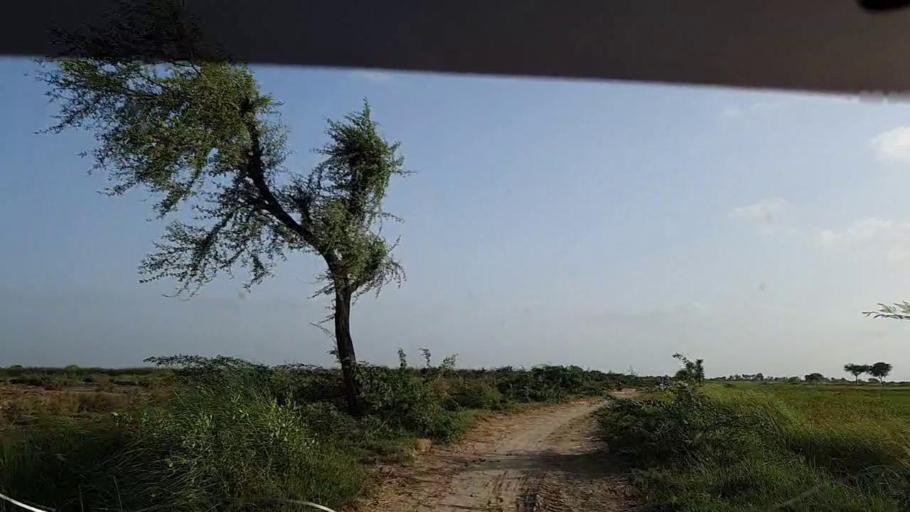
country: PK
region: Sindh
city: Badin
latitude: 24.5600
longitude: 68.8628
